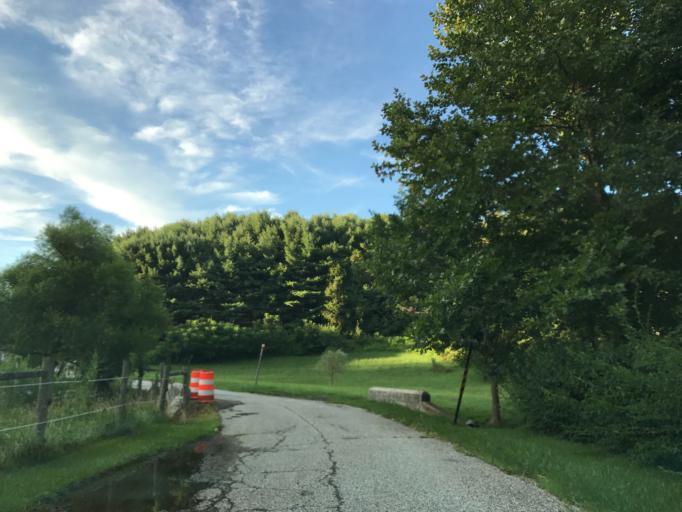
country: US
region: Pennsylvania
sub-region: York County
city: New Freedom
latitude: 39.7170
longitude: -76.6948
